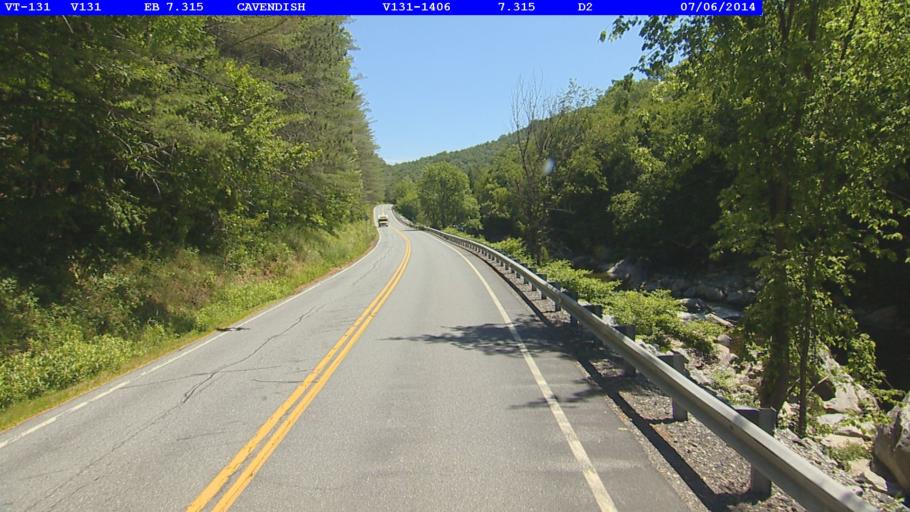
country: US
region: Vermont
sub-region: Windsor County
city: Springfield
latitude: 43.3929
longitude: -72.5445
